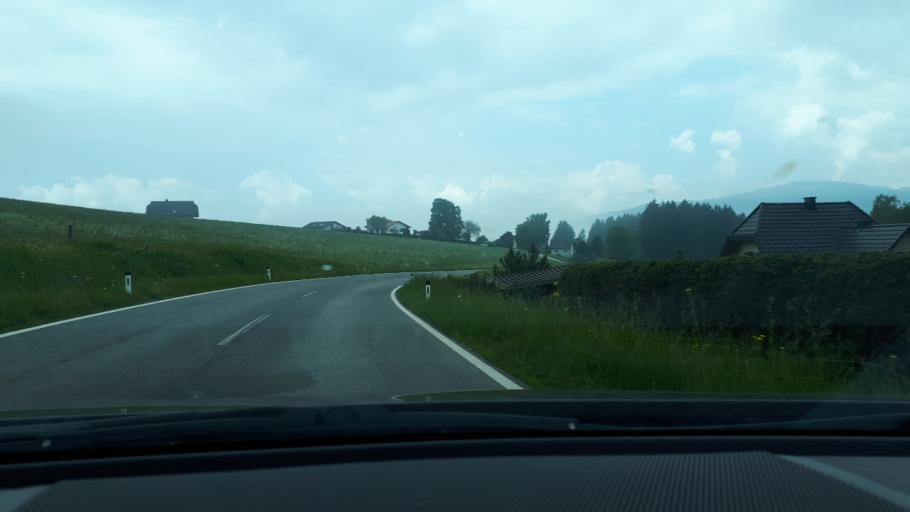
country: AT
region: Carinthia
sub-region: Politischer Bezirk Wolfsberg
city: Preitenegg
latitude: 46.9320
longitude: 14.9488
